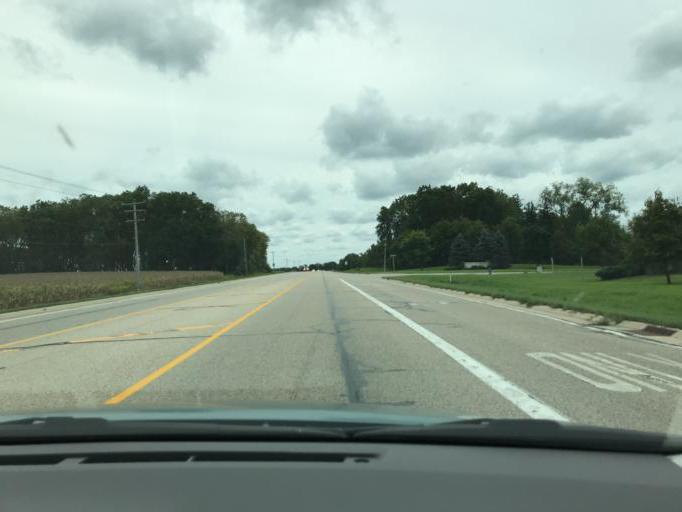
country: US
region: Wisconsin
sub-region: Racine County
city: Bohners Lake
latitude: 42.6464
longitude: -88.2535
